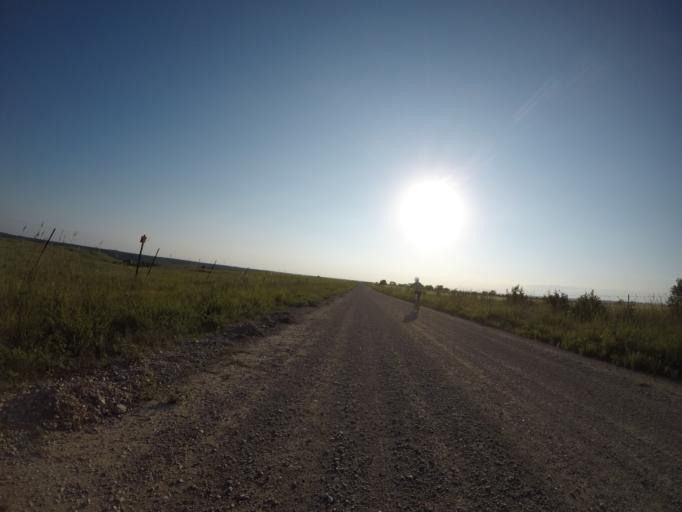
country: US
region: Kansas
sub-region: Riley County
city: Ogden
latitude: 39.0481
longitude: -96.6918
